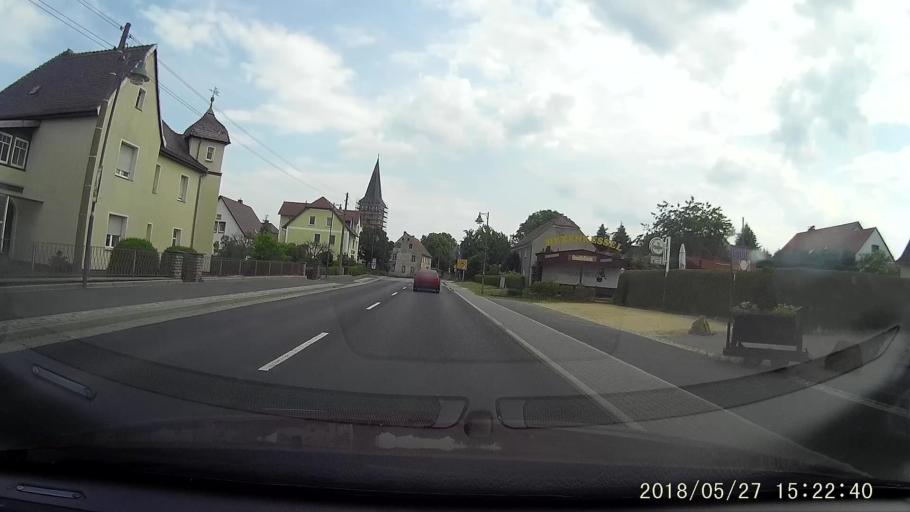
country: DE
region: Saxony
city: Kodersdorf
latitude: 51.2317
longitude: 14.8921
